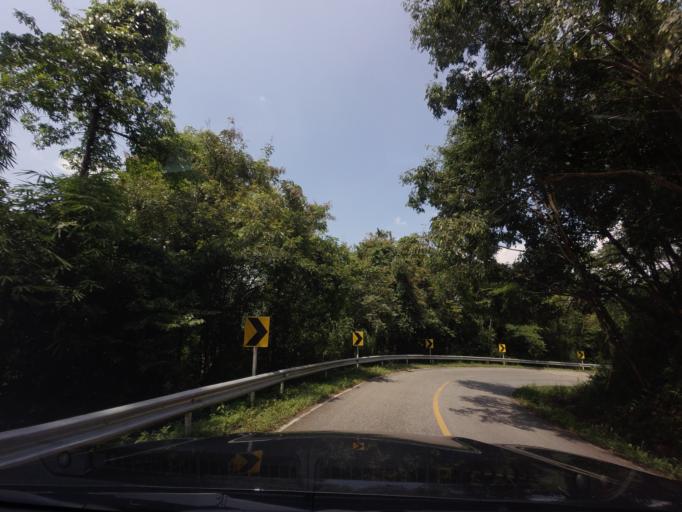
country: TH
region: Loei
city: Na Haeo
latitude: 17.6086
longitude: 100.8935
